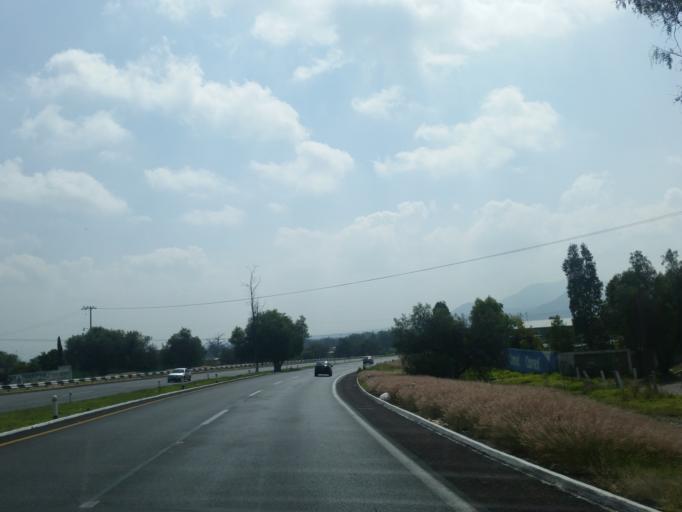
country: MX
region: Mexico
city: Acolman
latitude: 19.6278
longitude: -98.9283
